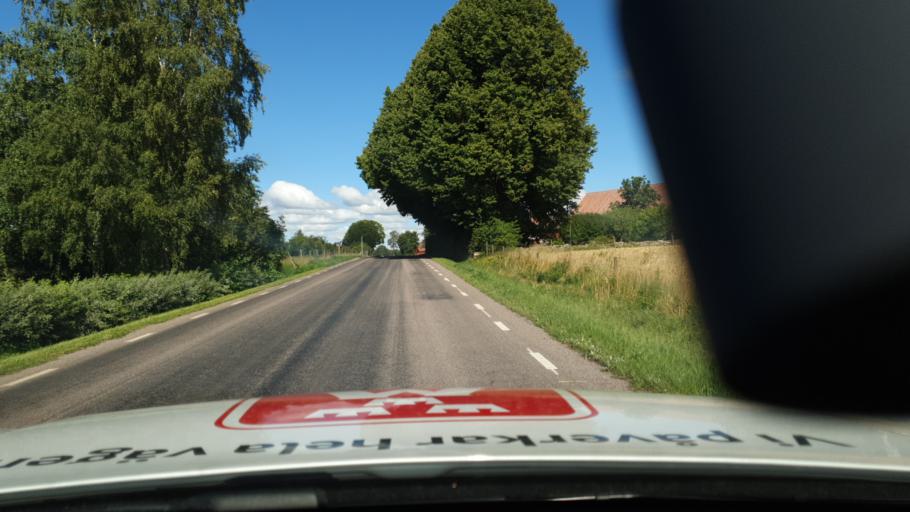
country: SE
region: Vaestra Goetaland
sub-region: Falkopings Kommun
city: Falkoeping
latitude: 58.2138
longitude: 13.5854
